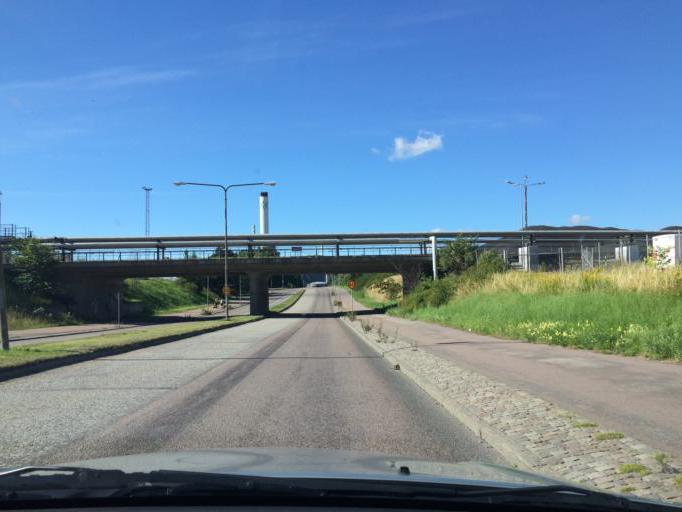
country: SE
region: Vaestmanland
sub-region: Vasteras
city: Vasteras
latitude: 59.5947
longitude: 16.5224
